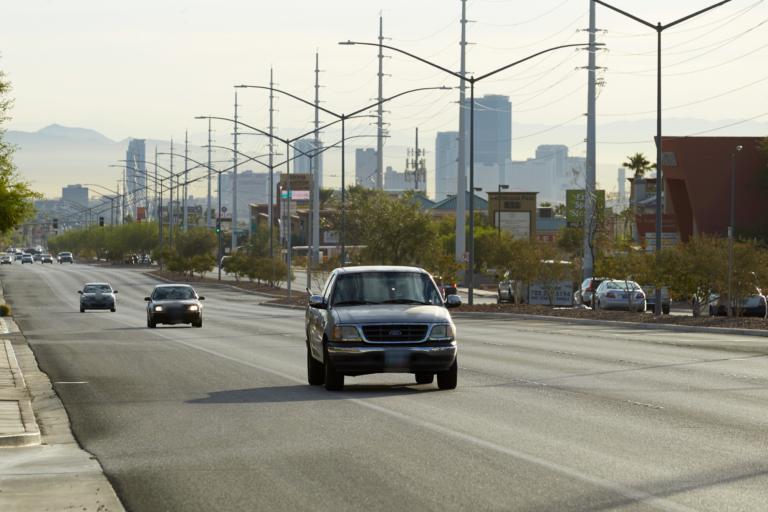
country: US
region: Nevada
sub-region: Clark County
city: Spring Valley
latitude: 36.1439
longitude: -115.2596
